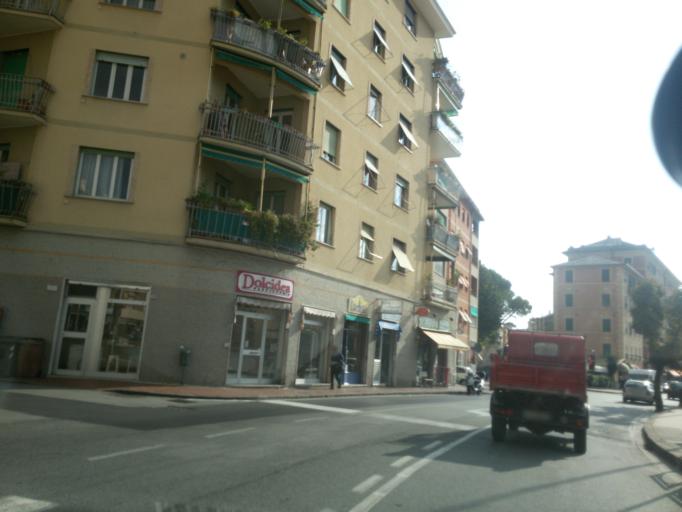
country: IT
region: Liguria
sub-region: Provincia di Genova
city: Recco
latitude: 44.3646
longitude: 9.1467
